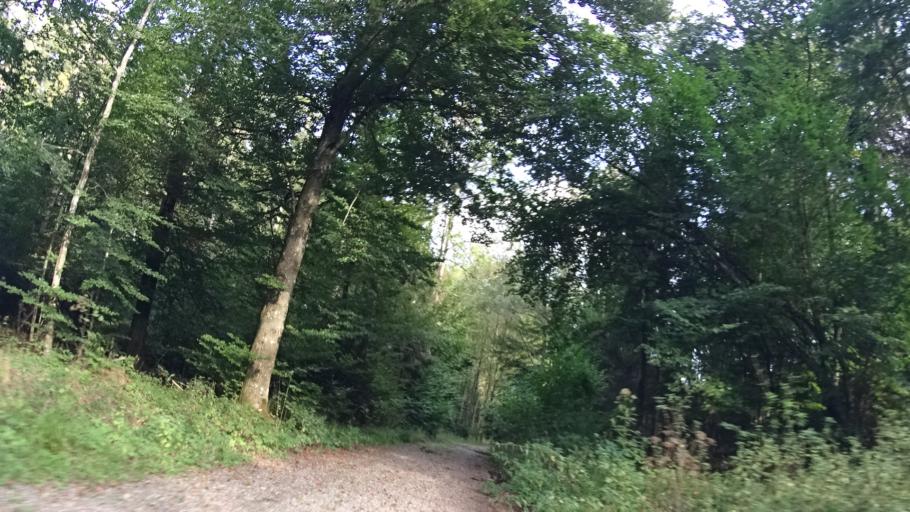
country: DE
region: Bavaria
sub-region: Lower Bavaria
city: Riedenburg
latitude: 48.9459
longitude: 11.6686
